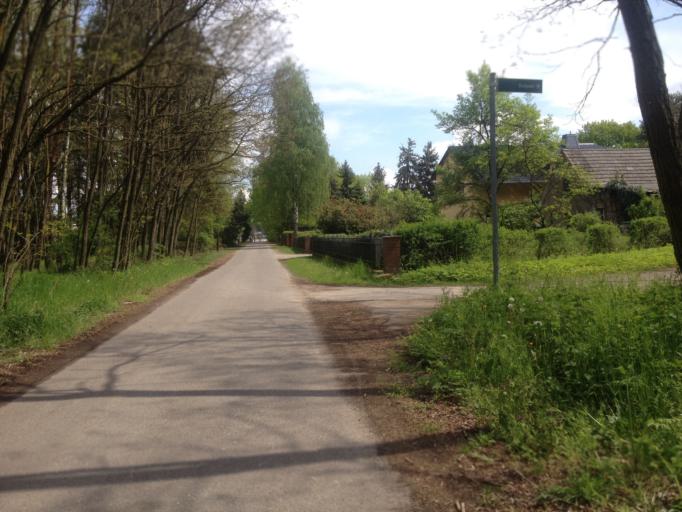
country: DE
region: Brandenburg
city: Cottbus
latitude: 51.7970
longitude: 14.2959
